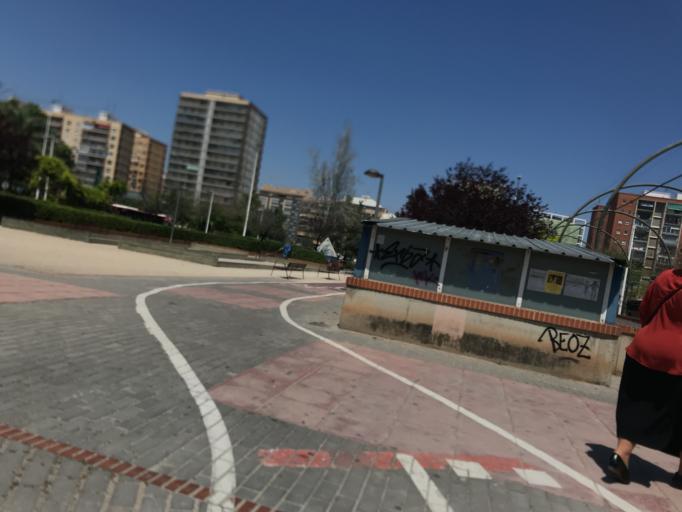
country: ES
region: Valencia
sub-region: Provincia de Valencia
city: Mislata
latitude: 39.4685
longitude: -0.4058
